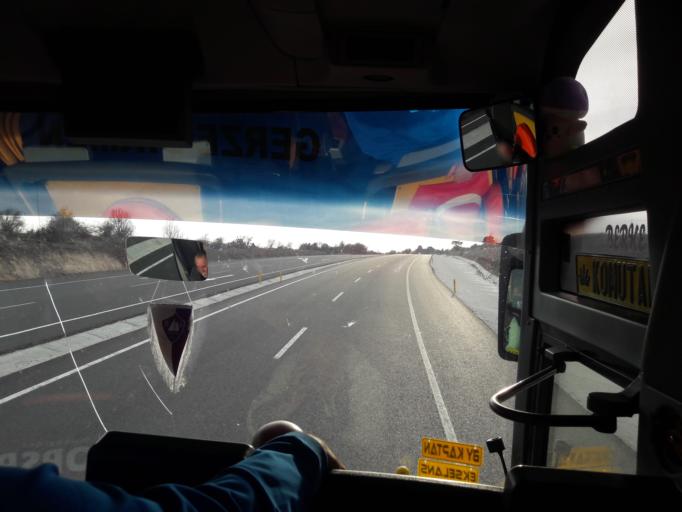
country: TR
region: Cankiri
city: Ilgaz
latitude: 40.8590
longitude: 33.6224
